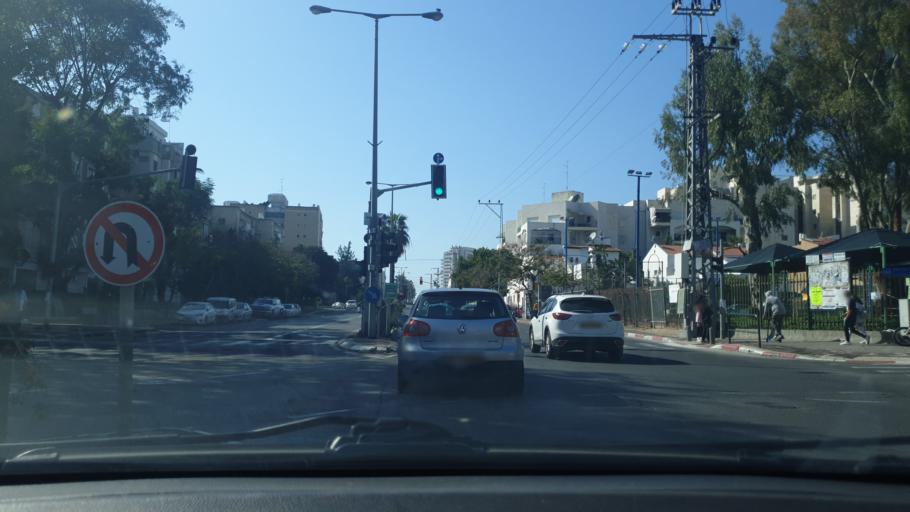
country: IL
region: Tel Aviv
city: Azor
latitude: 32.0455
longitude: 34.8064
